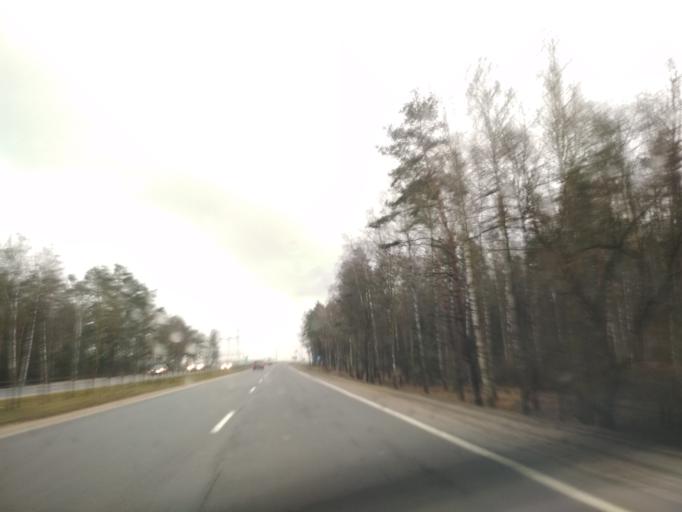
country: BY
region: Minsk
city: Dukora
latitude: 53.6216
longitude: 28.0448
